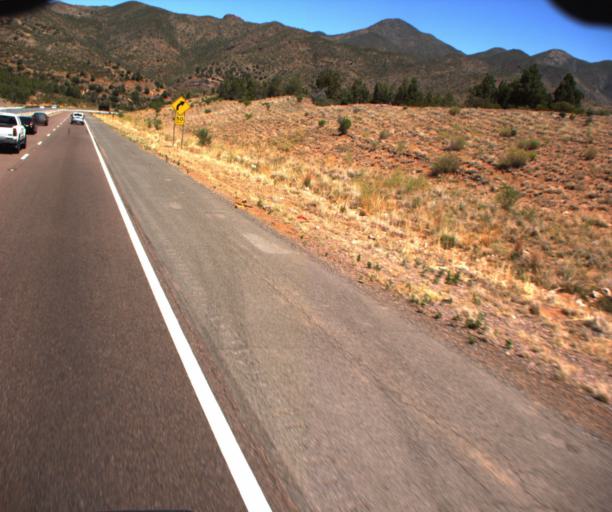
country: US
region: Arizona
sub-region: Gila County
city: Tonto Basin
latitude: 33.9396
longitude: -111.4407
